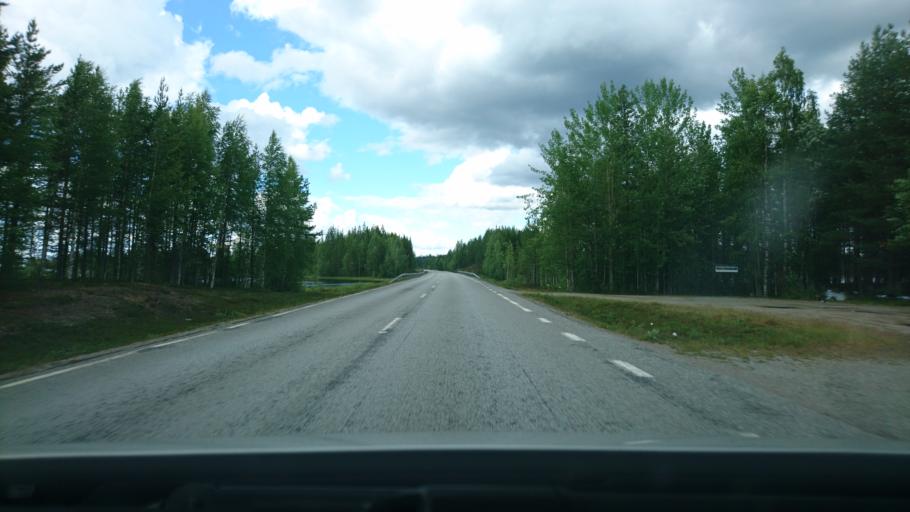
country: SE
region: Vaesterbotten
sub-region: Asele Kommun
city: Asele
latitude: 63.8937
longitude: 17.2176
